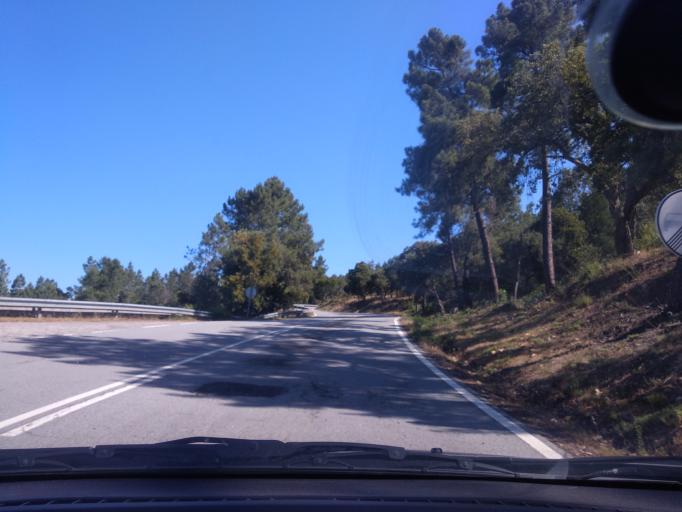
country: PT
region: Portalegre
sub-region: Nisa
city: Nisa
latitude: 39.6024
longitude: -7.6603
